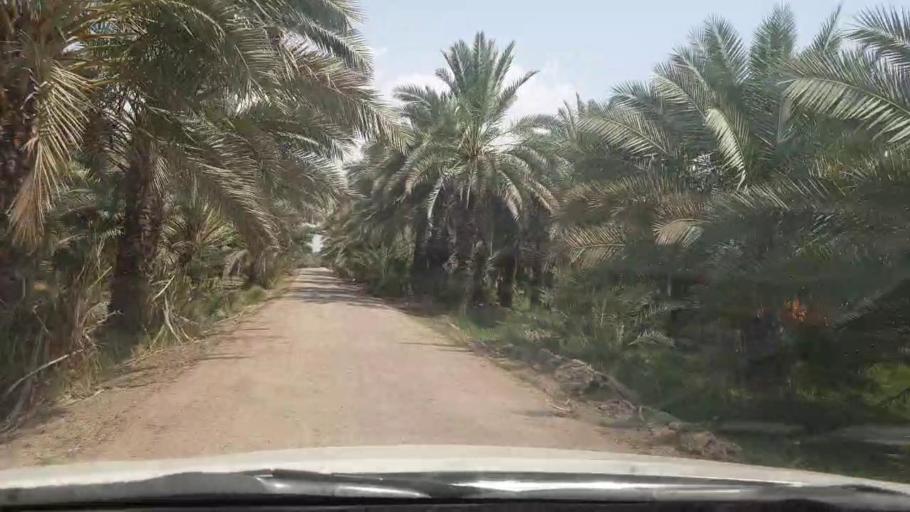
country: PK
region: Sindh
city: Khairpur
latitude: 27.5549
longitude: 68.8427
